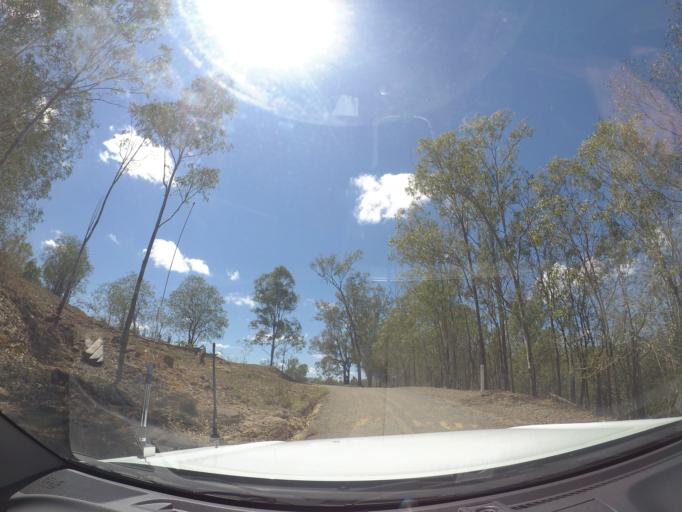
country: AU
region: Queensland
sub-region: Logan
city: Cedar Vale
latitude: -27.8593
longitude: 152.8557
